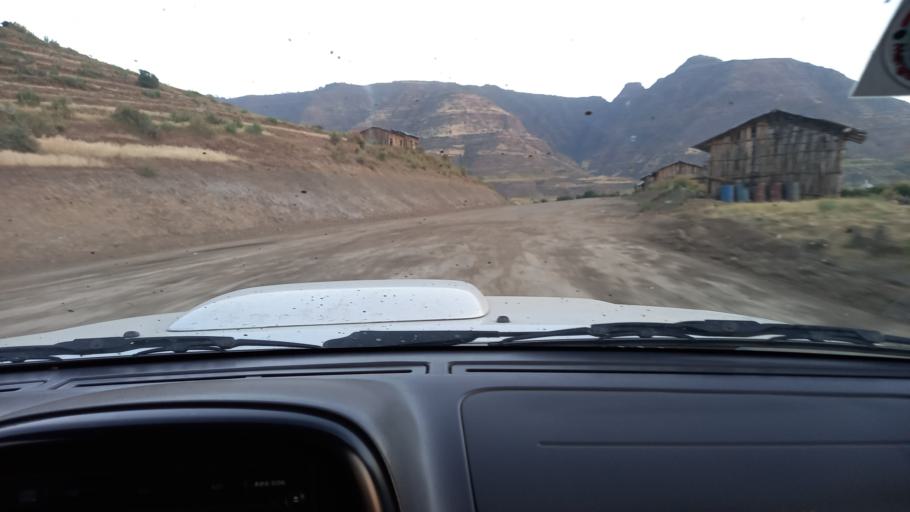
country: ET
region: Amhara
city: Debark'
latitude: 13.0374
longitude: 38.0405
